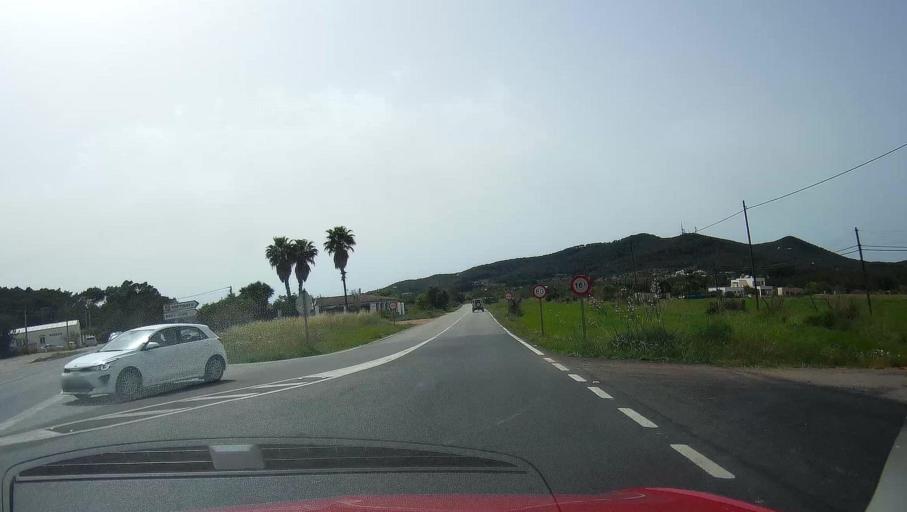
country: ES
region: Balearic Islands
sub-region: Illes Balears
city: Santa Eularia des Riu
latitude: 38.9854
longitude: 1.4965
